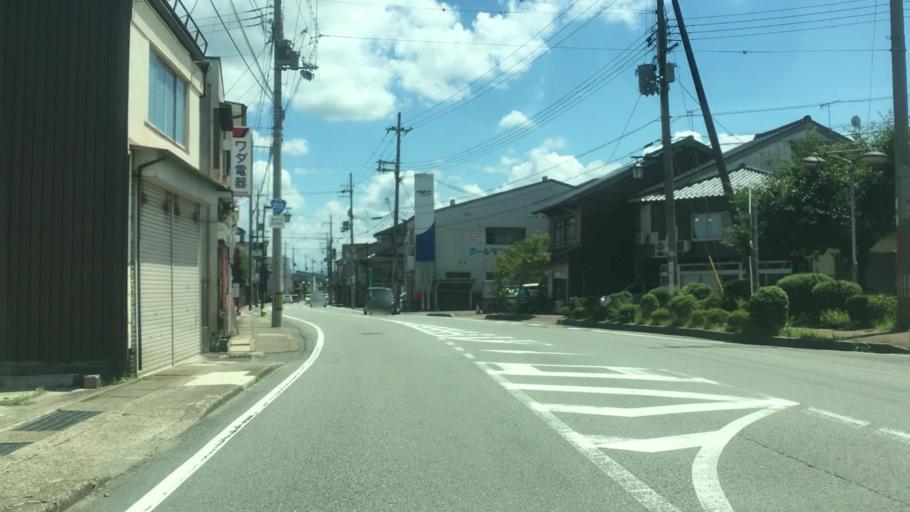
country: JP
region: Hyogo
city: Toyooka
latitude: 35.5391
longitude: 134.8244
